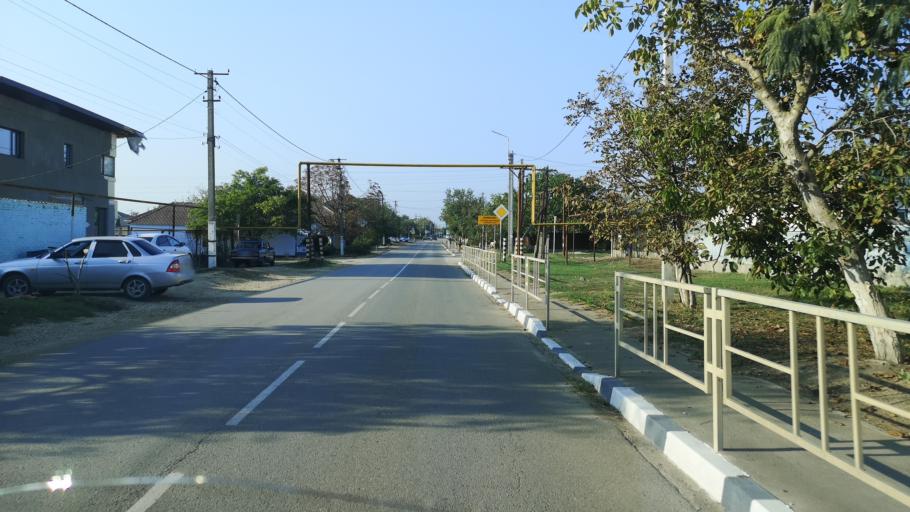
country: RU
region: Krasnodarskiy
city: Taman'
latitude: 45.2123
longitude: 36.7008
